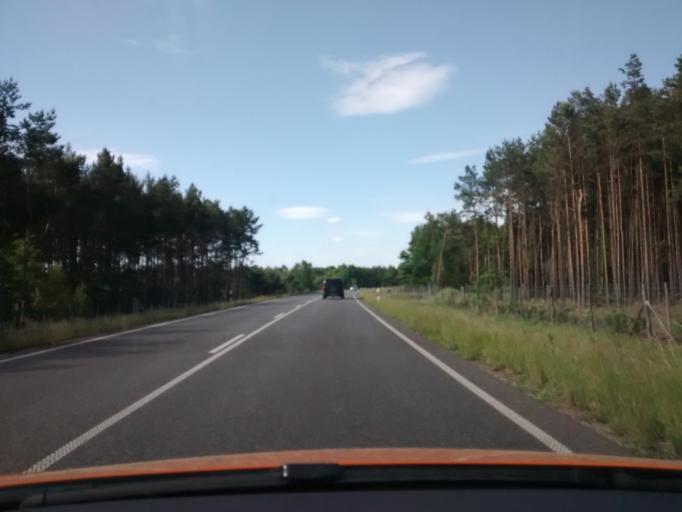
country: DE
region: Brandenburg
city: Juterbog
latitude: 52.0525
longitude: 13.1047
